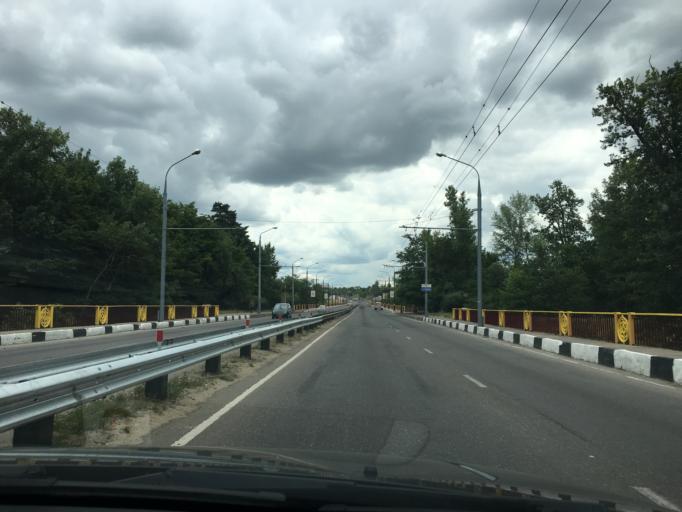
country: BY
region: Grodnenskaya
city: Hrodna
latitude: 53.6580
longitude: 23.8584
